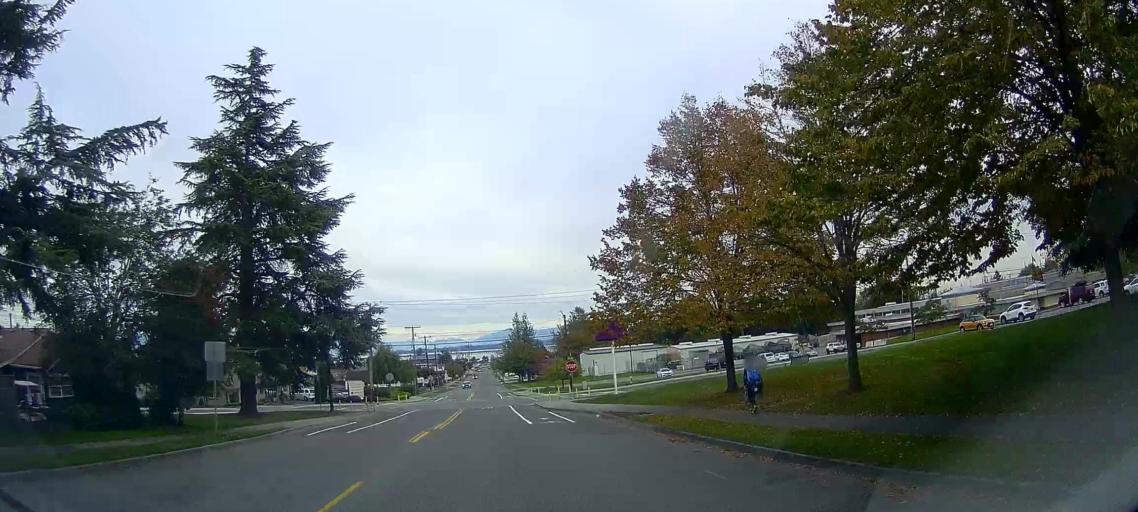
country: US
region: Washington
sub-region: Skagit County
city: Anacortes
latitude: 48.5047
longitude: -122.6183
